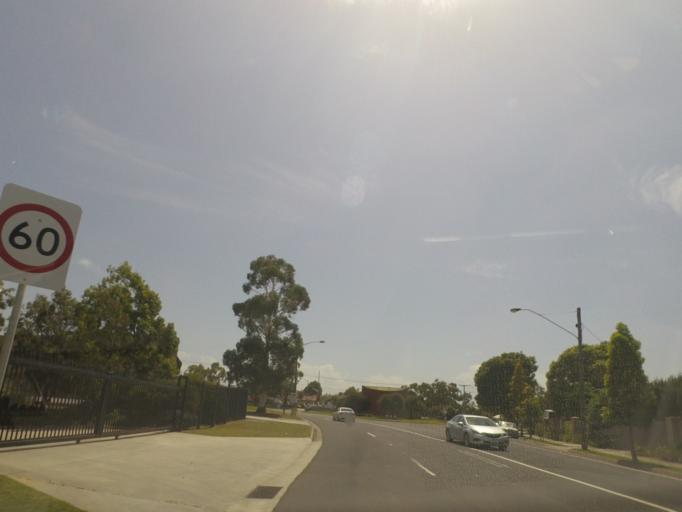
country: AU
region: Victoria
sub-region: Greater Dandenong
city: Springvale South
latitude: -37.9607
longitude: 145.1301
